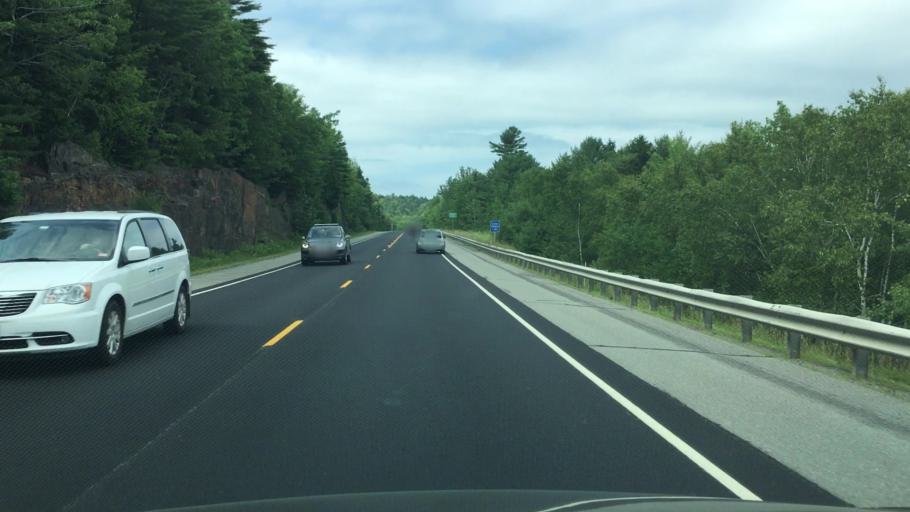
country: US
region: Maine
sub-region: Hancock County
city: Bucksport
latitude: 44.5482
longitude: -68.8093
